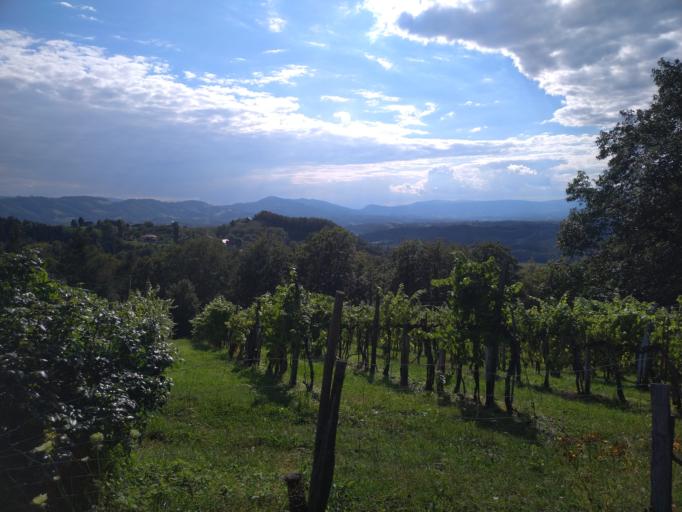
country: AT
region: Styria
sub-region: Politischer Bezirk Leibnitz
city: Sankt Johann im Saggautal
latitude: 46.7142
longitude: 15.4248
